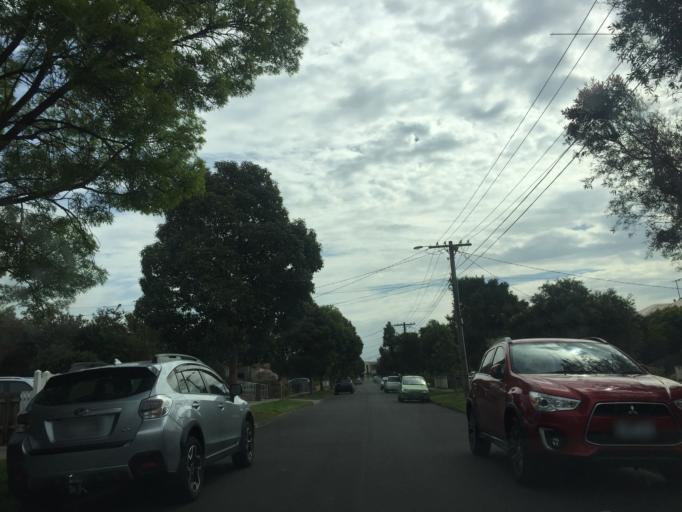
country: AU
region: Victoria
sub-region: Darebin
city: Preston
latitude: -37.7423
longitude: 145.0135
